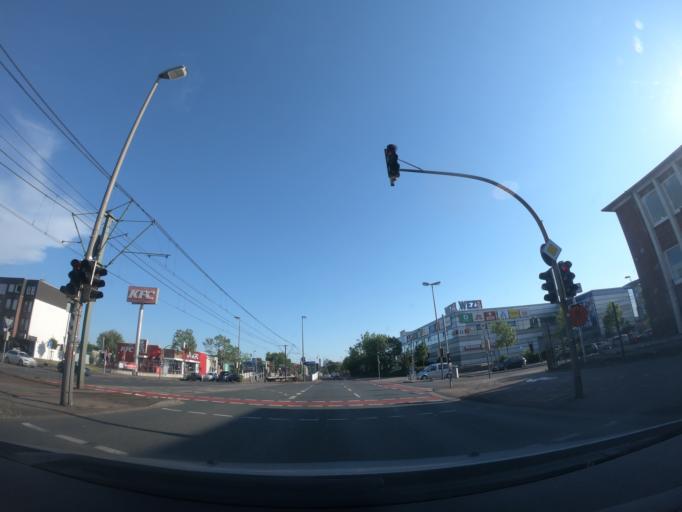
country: DE
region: North Rhine-Westphalia
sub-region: Regierungsbezirk Arnsberg
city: Dortmund
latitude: 51.5315
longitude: 7.4730
